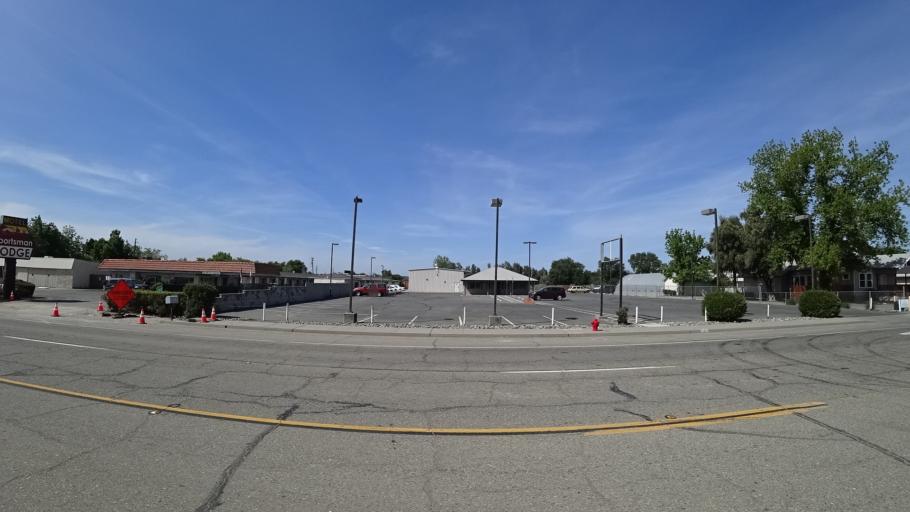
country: US
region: California
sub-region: Tehama County
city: Red Bluff
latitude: 40.1858
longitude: -122.2000
